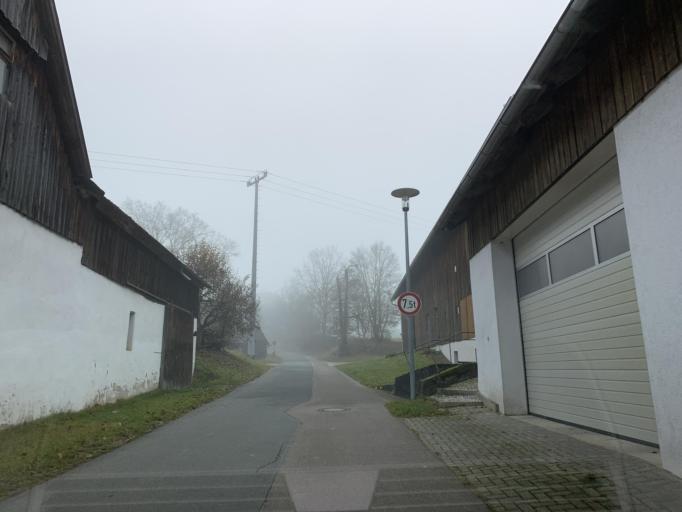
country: DE
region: Bavaria
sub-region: Upper Palatinate
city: Neunburg vorm Wald
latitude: 49.3563
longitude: 12.3790
